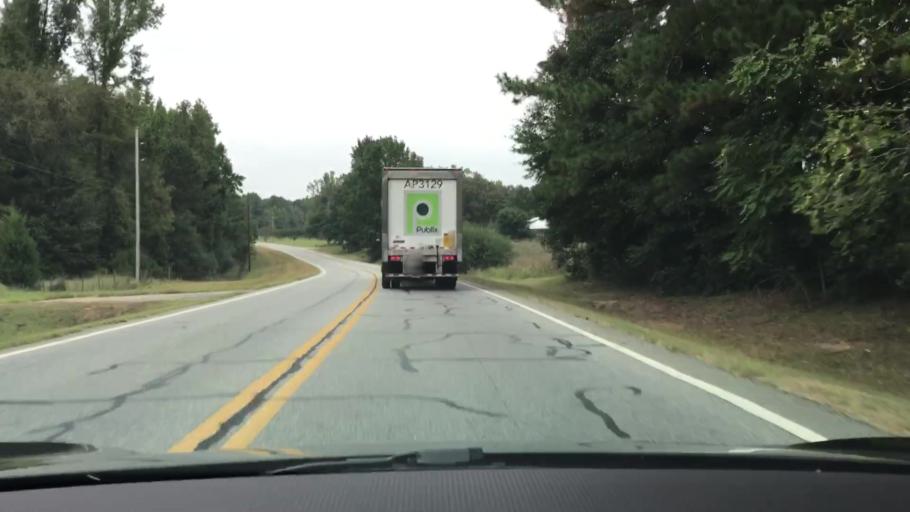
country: US
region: Georgia
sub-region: Oconee County
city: Watkinsville
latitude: 33.7489
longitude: -83.3011
